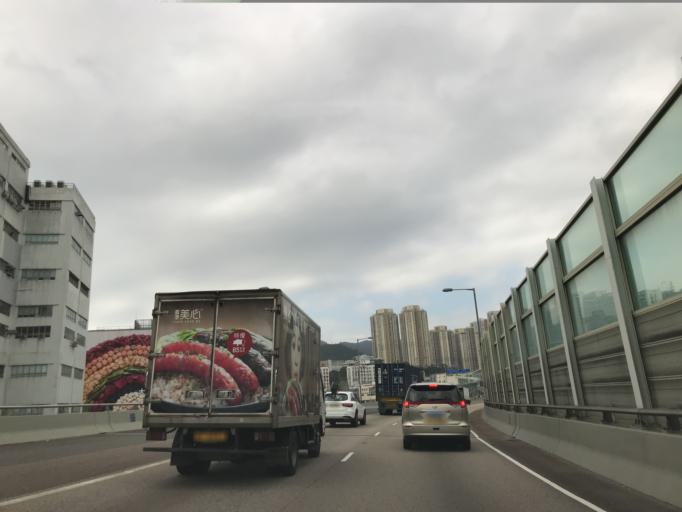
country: HK
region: Sha Tin
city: Sha Tin
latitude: 22.3772
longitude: 114.1814
